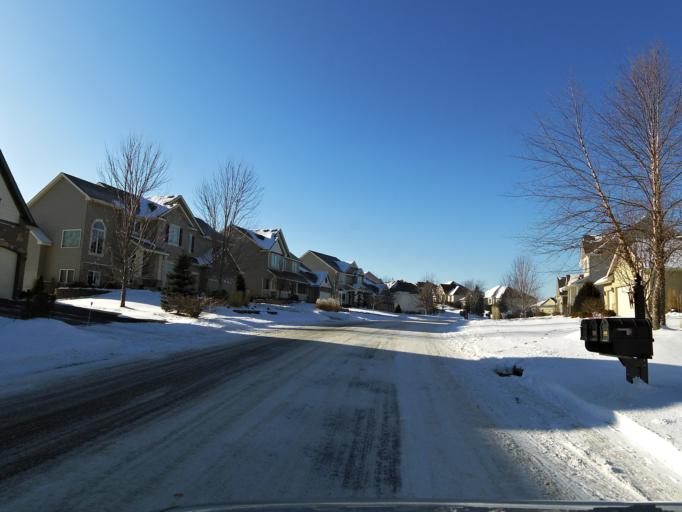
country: US
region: Minnesota
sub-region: Scott County
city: Prior Lake
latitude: 44.7277
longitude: -93.4536
